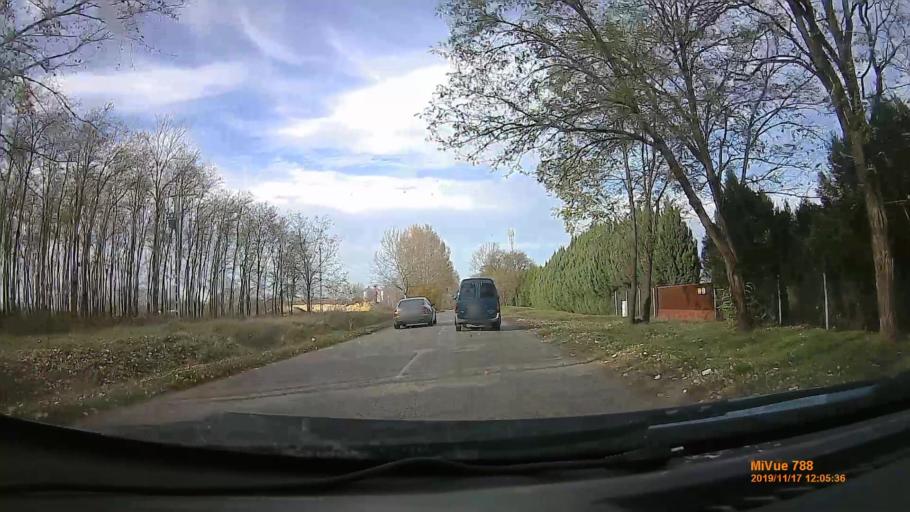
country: HU
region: Bacs-Kiskun
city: Szentkiraly
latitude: 46.9093
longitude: 19.9190
